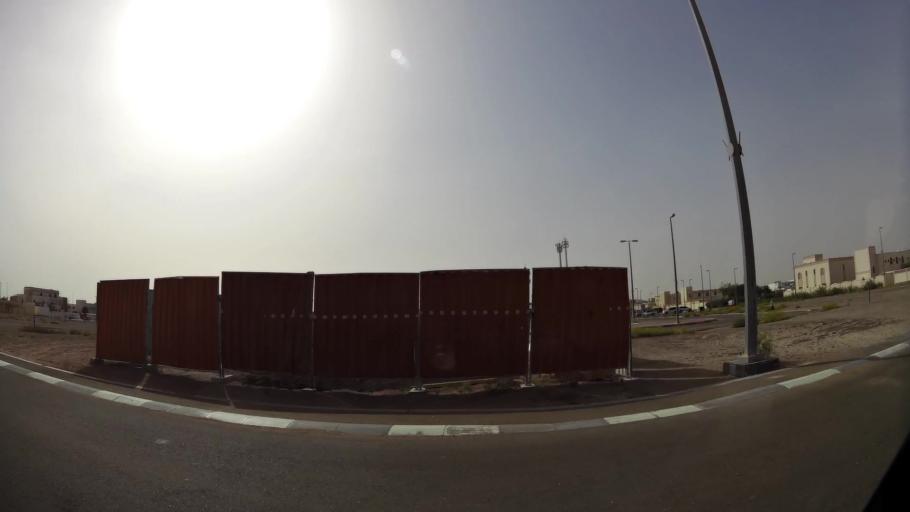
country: AE
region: Abu Dhabi
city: Al Ain
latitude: 24.2072
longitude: 55.5941
